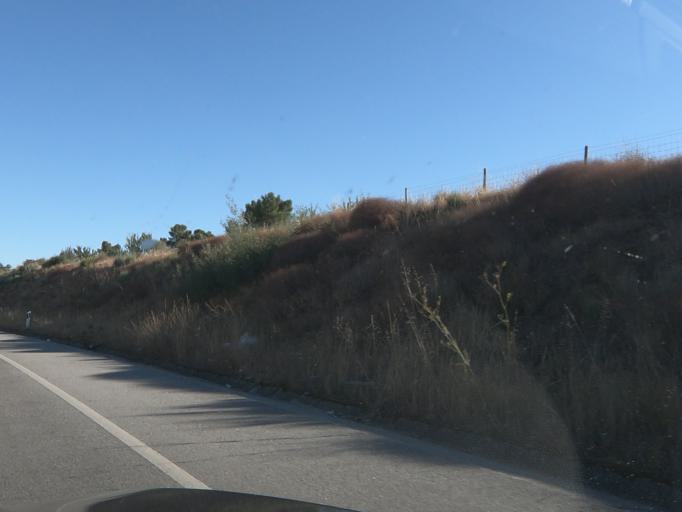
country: PT
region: Vila Real
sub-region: Valpacos
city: Valpacos
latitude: 41.5723
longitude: -7.2990
